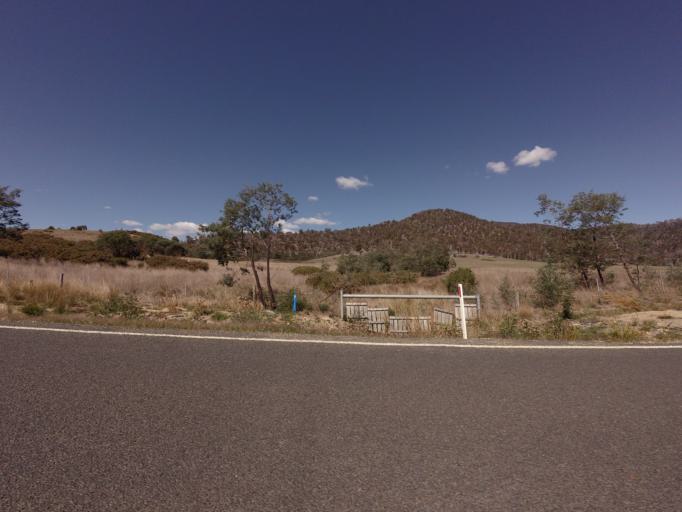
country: AU
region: Tasmania
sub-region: Break O'Day
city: St Helens
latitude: -41.6971
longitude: 147.8621
